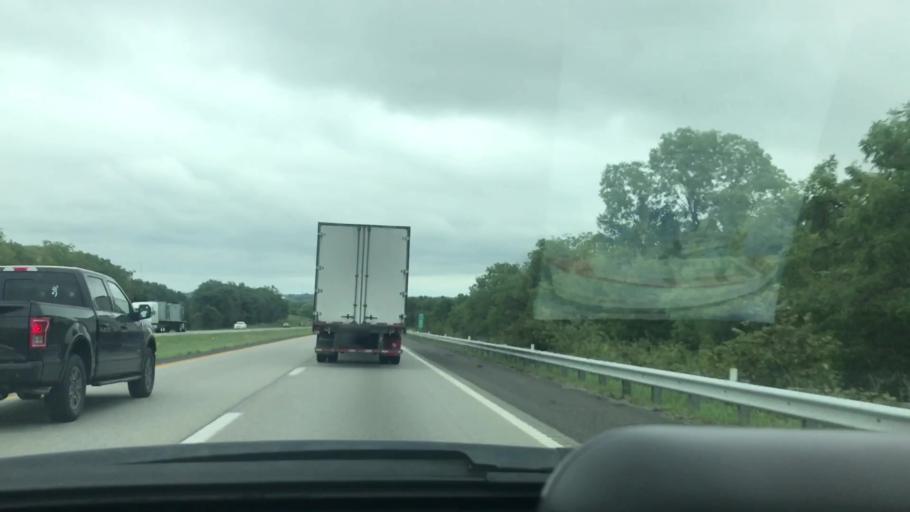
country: US
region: Missouri
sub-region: Greene County
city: Republic
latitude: 37.1856
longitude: -93.5484
